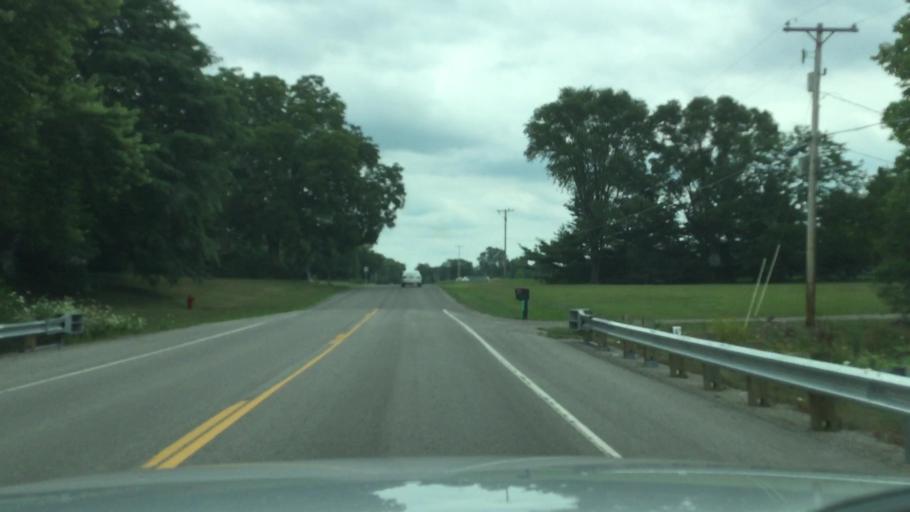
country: US
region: Michigan
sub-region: Saginaw County
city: Frankenmuth
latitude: 43.3217
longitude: -83.7931
